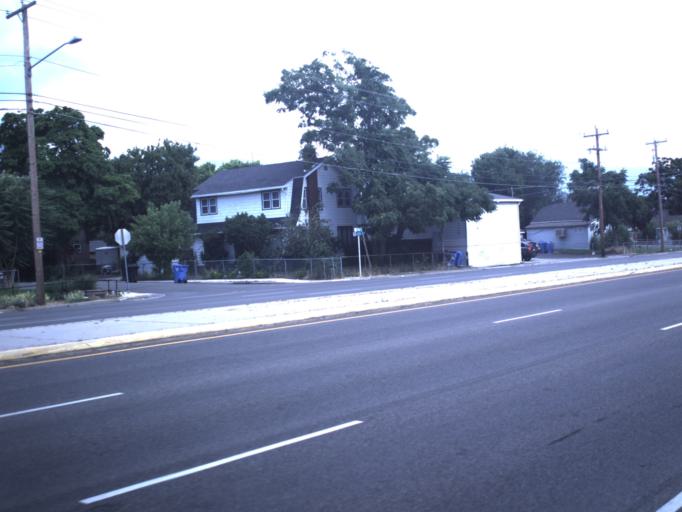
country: US
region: Utah
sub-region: Salt Lake County
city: Millcreek
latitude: 40.7026
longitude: -111.8715
